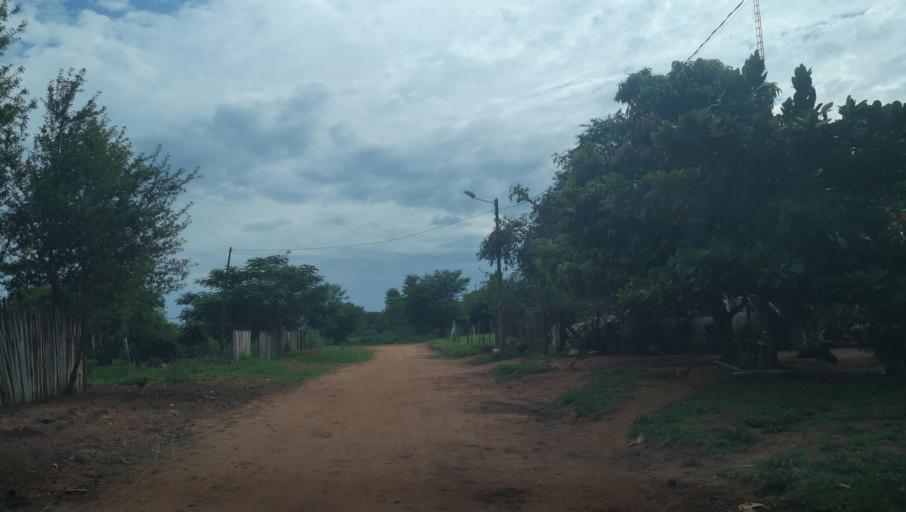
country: PY
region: San Pedro
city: Capiibary
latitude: -24.7213
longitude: -56.0195
